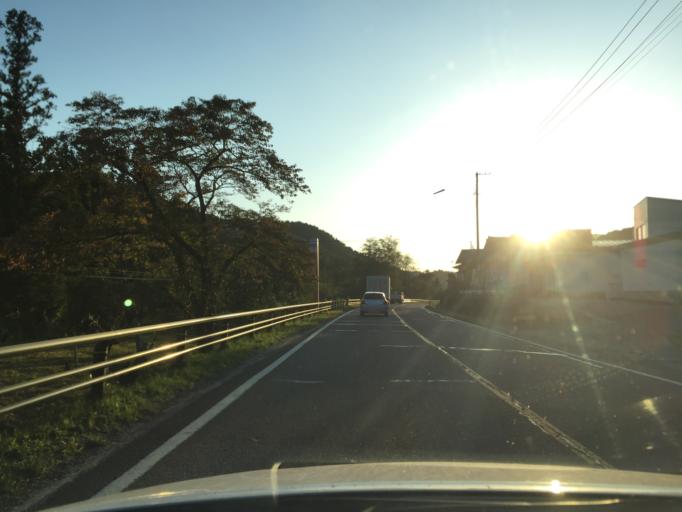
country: JP
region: Fukushima
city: Sukagawa
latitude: 37.3137
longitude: 140.4604
